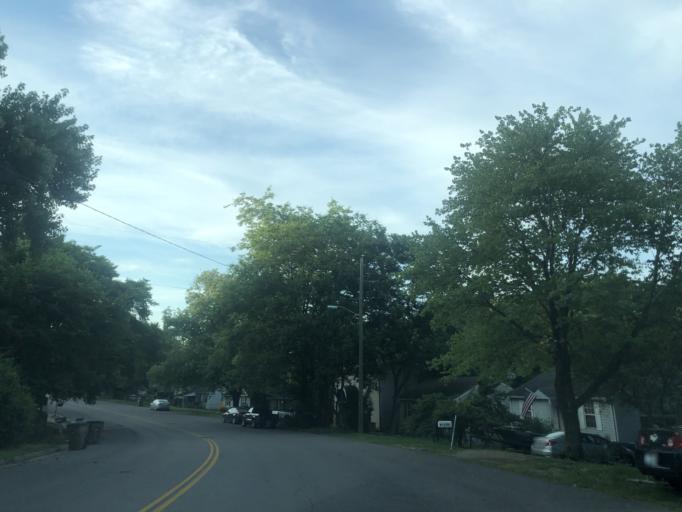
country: US
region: Tennessee
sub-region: Davidson County
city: Nashville
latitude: 36.1640
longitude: -86.7467
